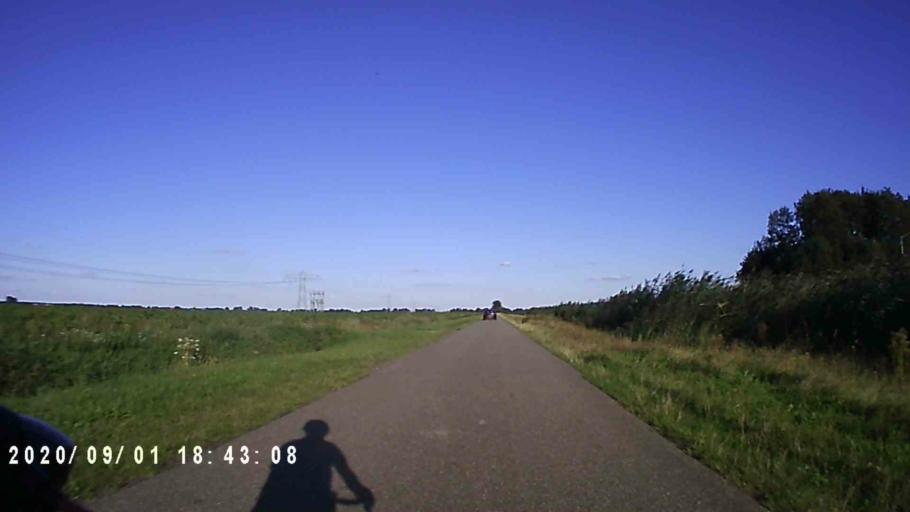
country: NL
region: Groningen
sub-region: Gemeente Hoogezand-Sappemeer
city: Sappemeer
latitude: 53.1459
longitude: 6.8302
